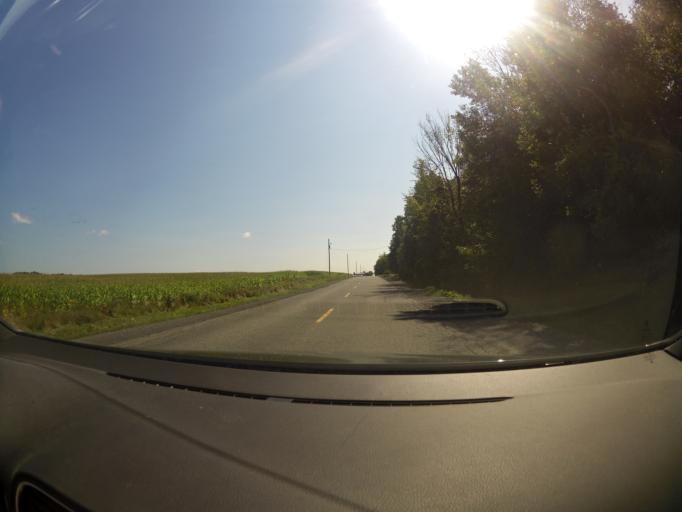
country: CA
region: Ontario
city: Arnprior
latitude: 45.3709
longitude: -76.2575
